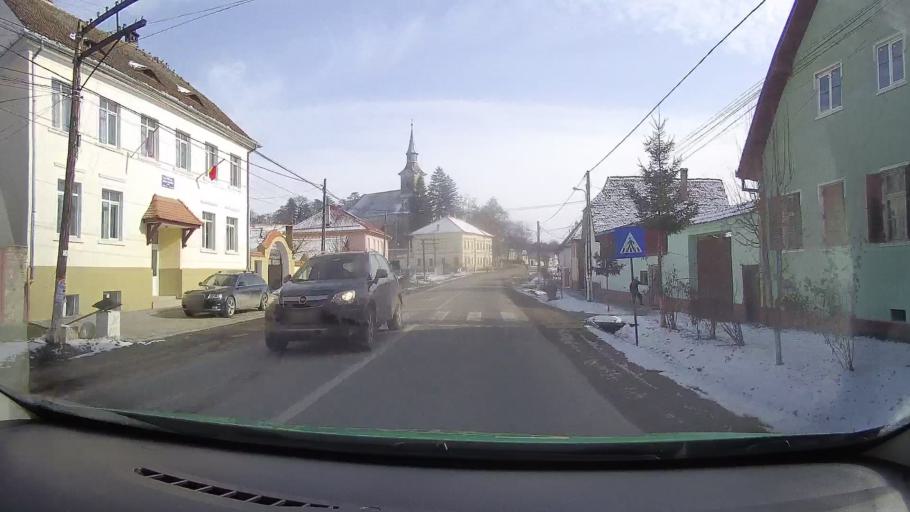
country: RO
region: Mures
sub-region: Comuna Apold
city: Saes
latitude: 46.1566
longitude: 24.7679
